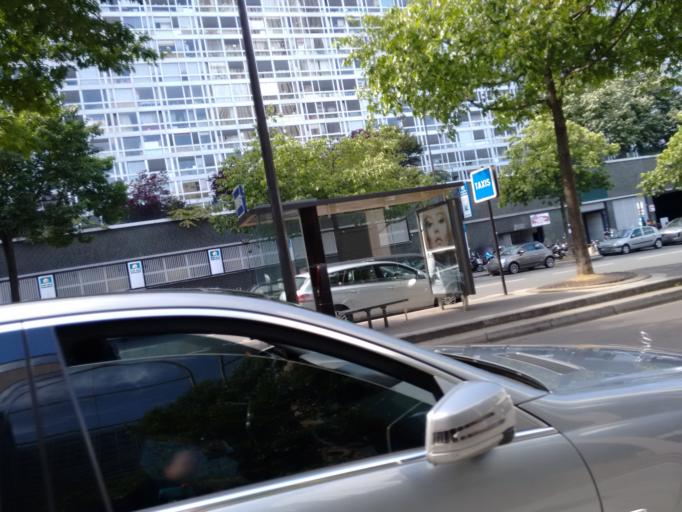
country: FR
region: Ile-de-France
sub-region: Departement des Hauts-de-Seine
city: Montrouge
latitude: 48.8386
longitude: 2.3195
